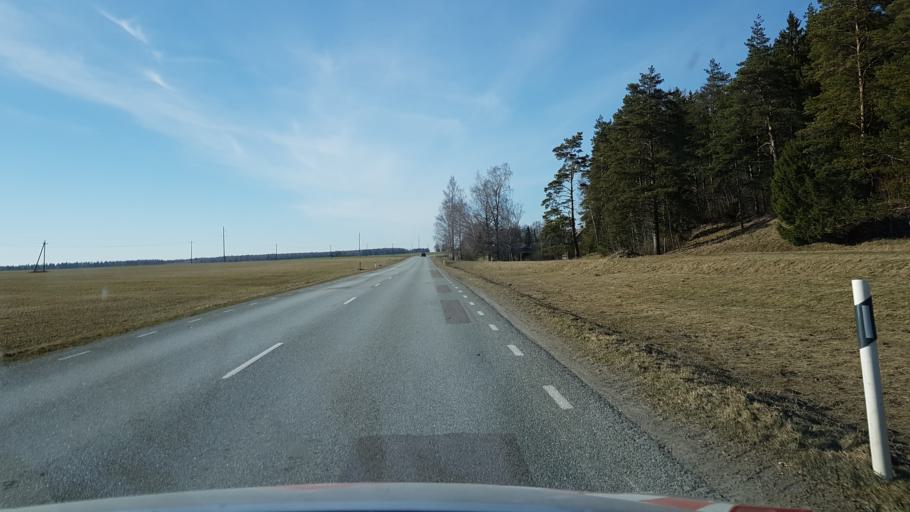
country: EE
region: Laeaene-Virumaa
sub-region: Vinni vald
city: Vinni
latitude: 59.1939
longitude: 26.5673
